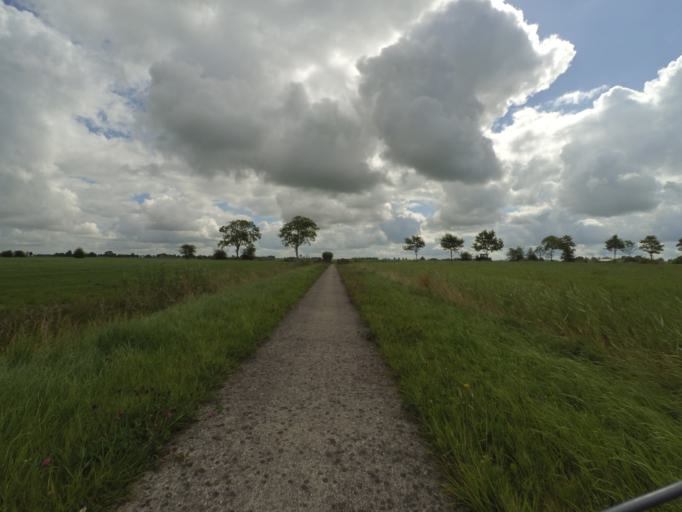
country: NL
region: Friesland
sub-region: Gemeente Kollumerland en Nieuwkruisland
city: Kollum
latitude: 53.2663
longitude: 6.1734
